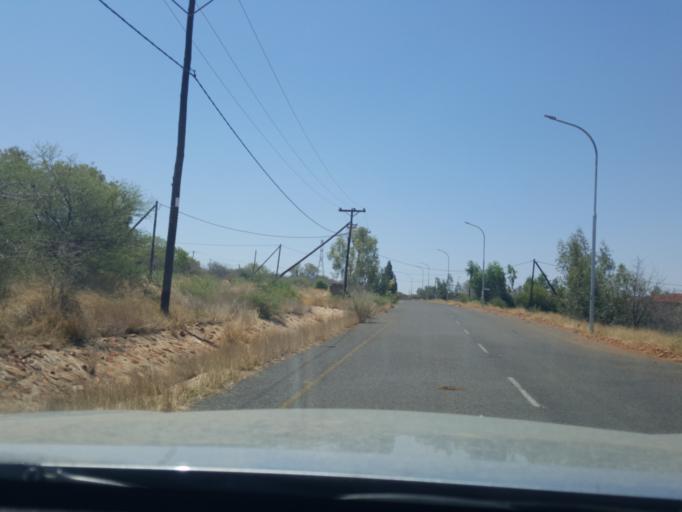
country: BW
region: South East
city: Lobatse
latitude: -25.1817
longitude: 25.6812
